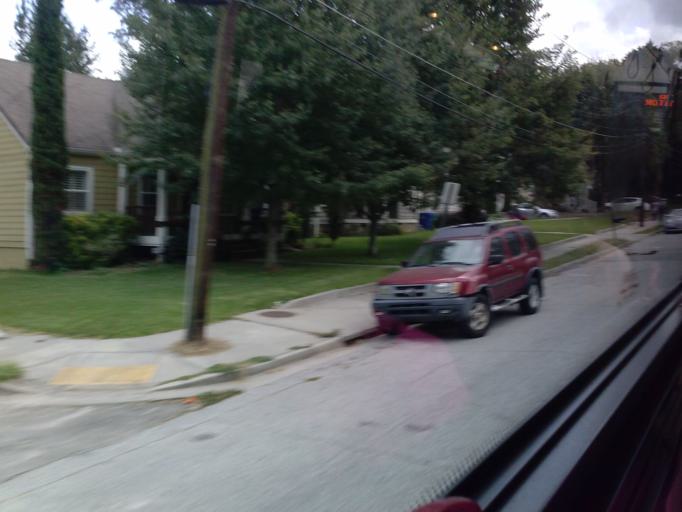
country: US
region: Georgia
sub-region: Fulton County
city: Atlanta
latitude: 33.7887
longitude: -84.3987
